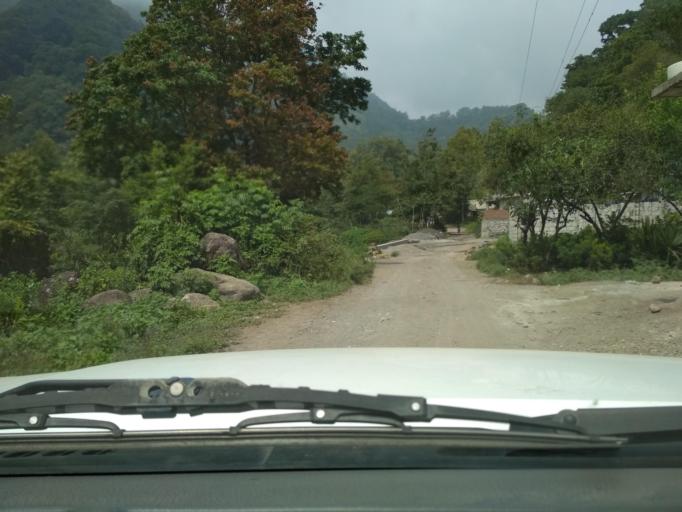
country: MX
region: Veracruz
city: Xocotla
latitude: 18.9891
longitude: -97.1117
